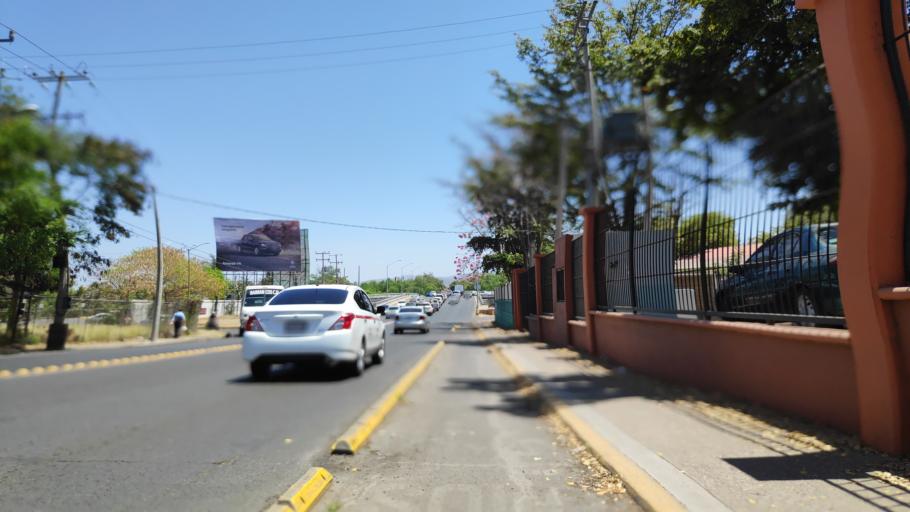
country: MX
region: Sinaloa
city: Culiacan
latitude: 24.8207
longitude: -107.3827
